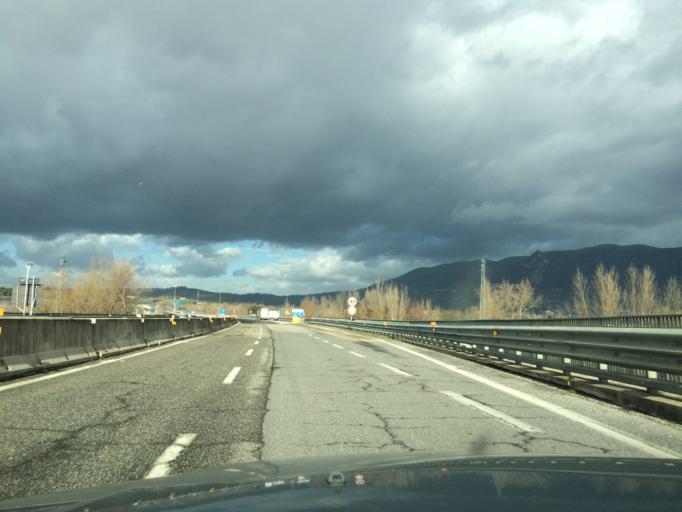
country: IT
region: Umbria
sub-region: Provincia di Terni
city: Terni
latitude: 42.5612
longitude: 12.5816
